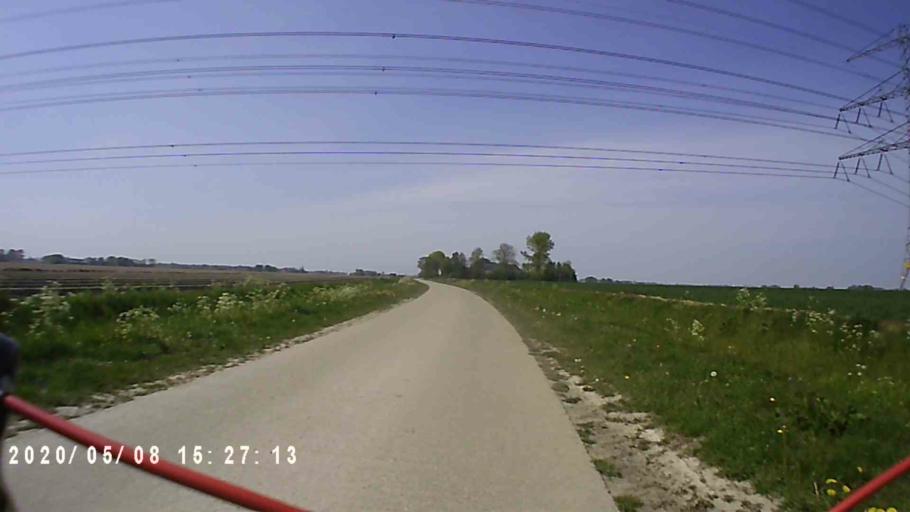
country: NL
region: Groningen
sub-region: Gemeente Appingedam
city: Appingedam
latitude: 53.3604
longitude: 6.7487
